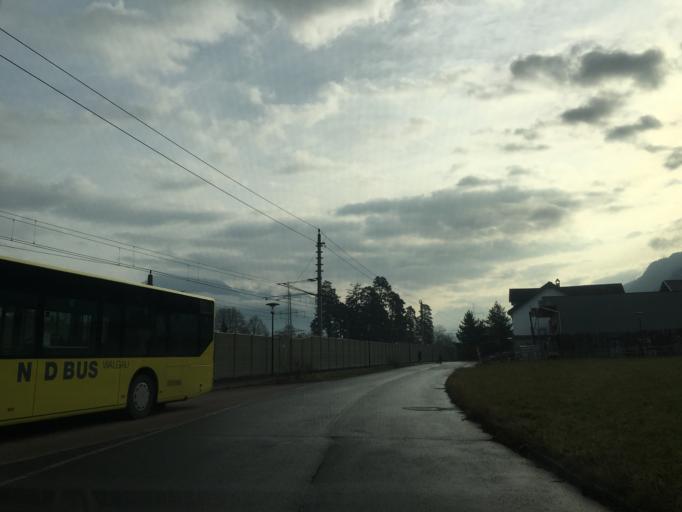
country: AT
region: Vorarlberg
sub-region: Politischer Bezirk Bludenz
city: Nenzing
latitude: 47.1908
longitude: 9.7097
